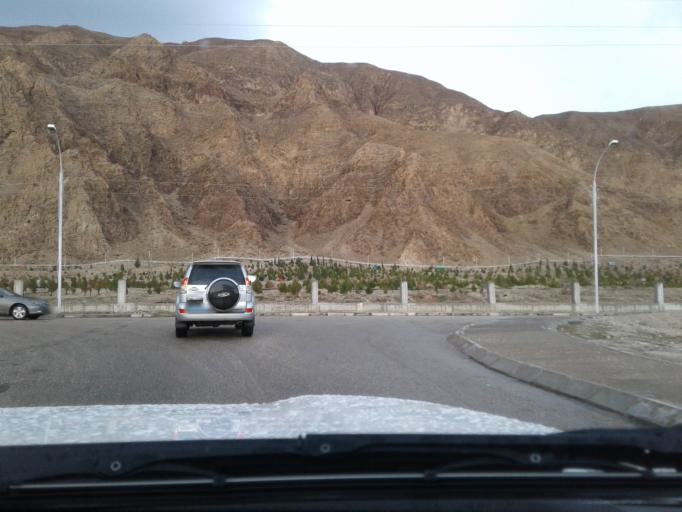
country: TM
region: Balkan
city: Balkanabat
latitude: 39.5276
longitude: 54.3610
